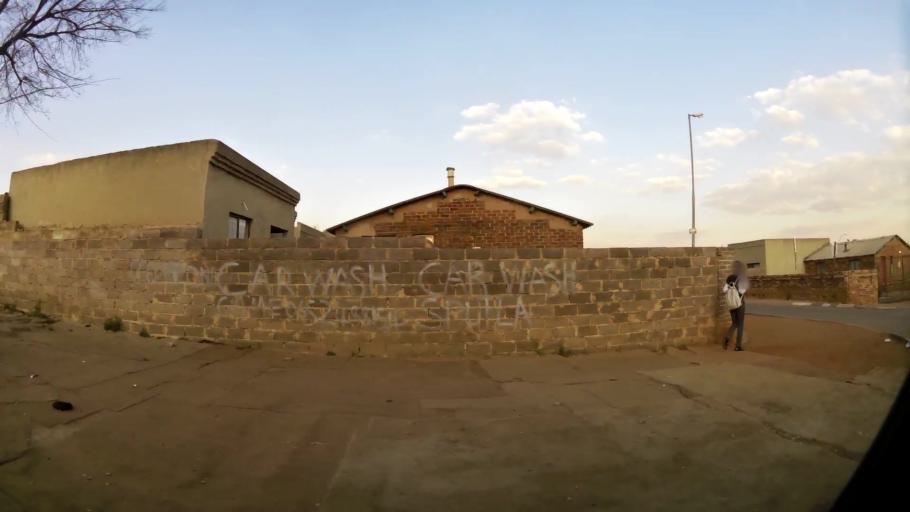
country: ZA
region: Gauteng
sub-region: City of Johannesburg Metropolitan Municipality
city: Roodepoort
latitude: -26.2170
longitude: 27.8931
